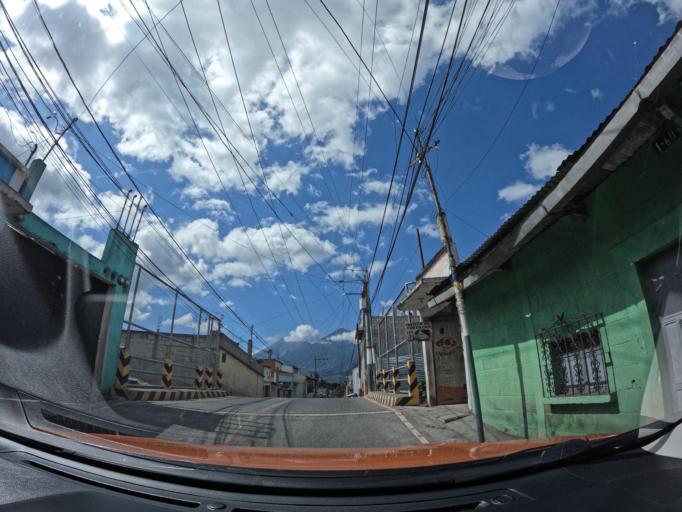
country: GT
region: Sacatepequez
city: Ciudad Vieja
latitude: 14.5258
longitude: -90.7543
